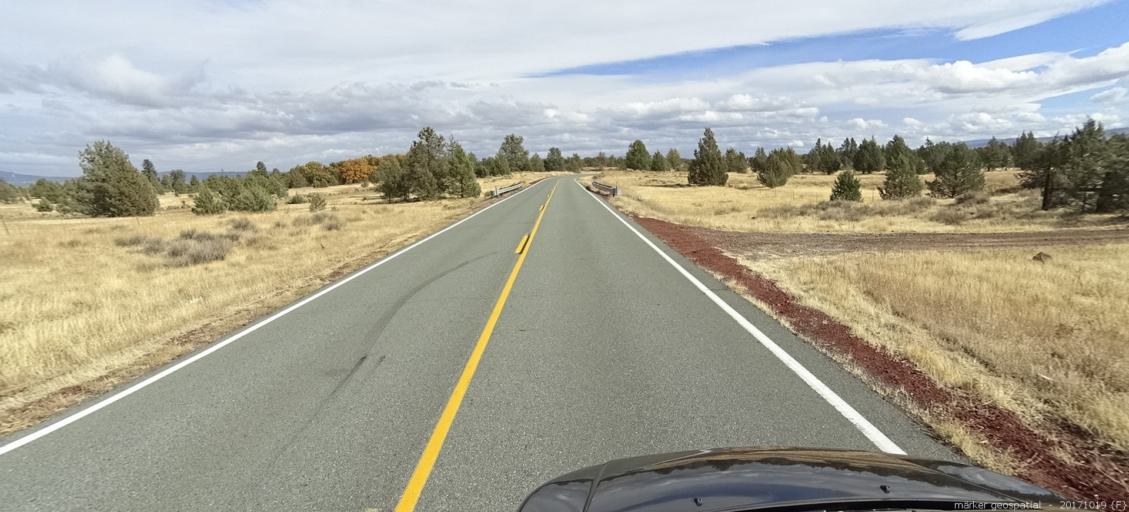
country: US
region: California
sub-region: Shasta County
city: Burney
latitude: 41.0082
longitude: -121.4591
